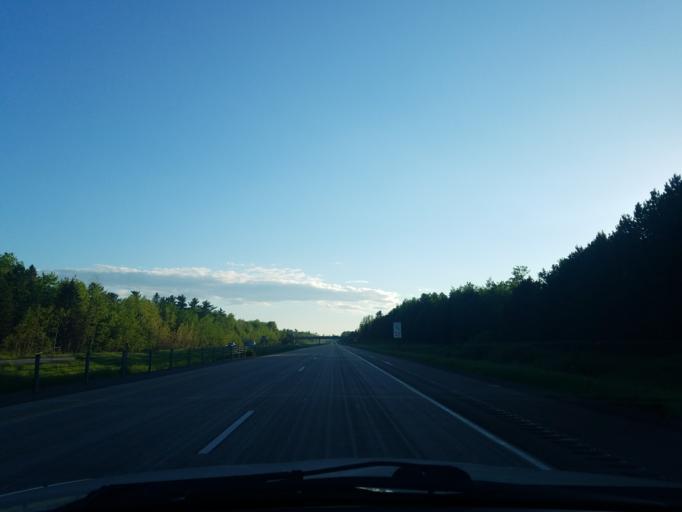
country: US
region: Minnesota
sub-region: Carlton County
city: Esko
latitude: 46.7012
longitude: -92.3153
